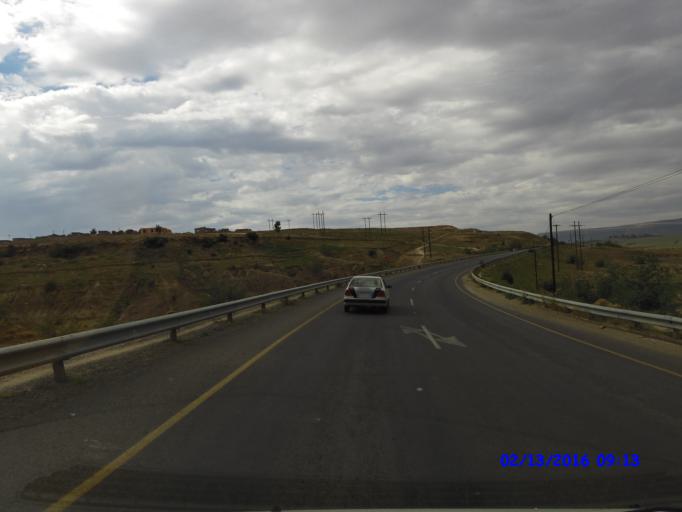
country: LS
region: Maseru
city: Maseru
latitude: -29.3814
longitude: 27.5034
